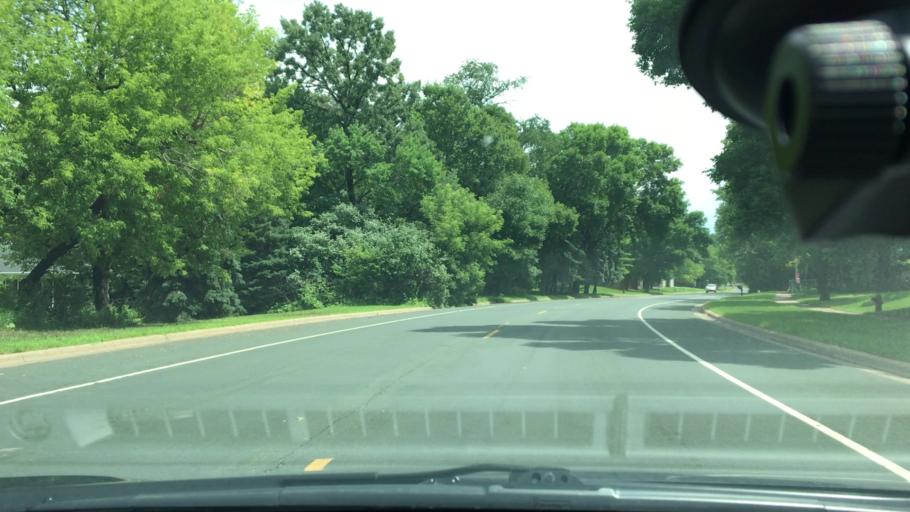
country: US
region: Minnesota
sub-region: Hennepin County
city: Maple Grove
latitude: 45.0676
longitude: -93.4393
